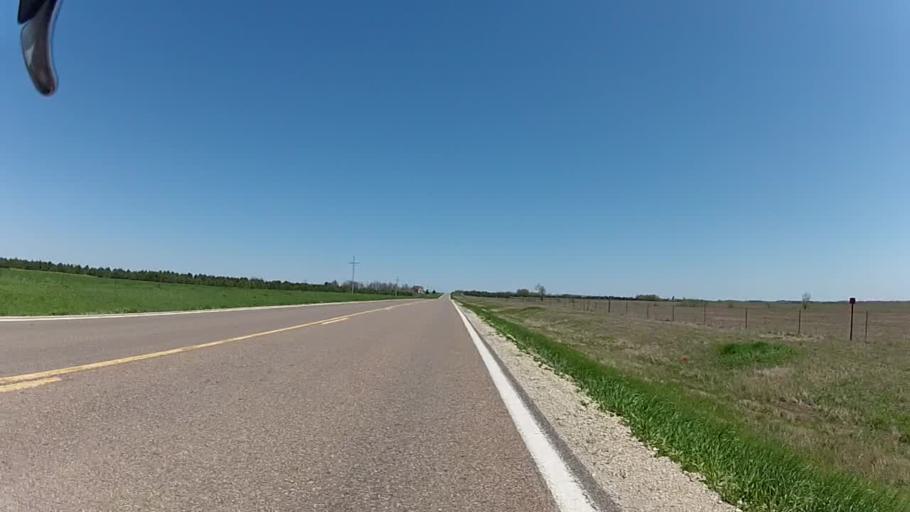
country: US
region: Kansas
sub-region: Riley County
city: Manhattan
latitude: 38.9521
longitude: -96.5202
